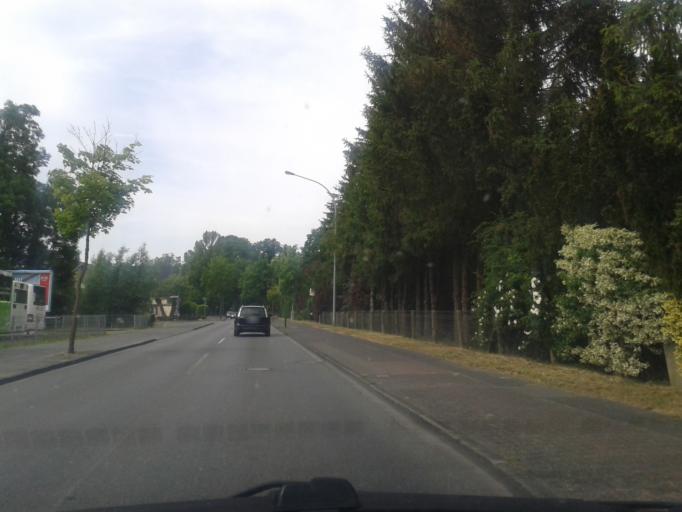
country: DE
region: North Rhine-Westphalia
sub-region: Regierungsbezirk Detmold
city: Paderborn
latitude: 51.7457
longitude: 8.7316
